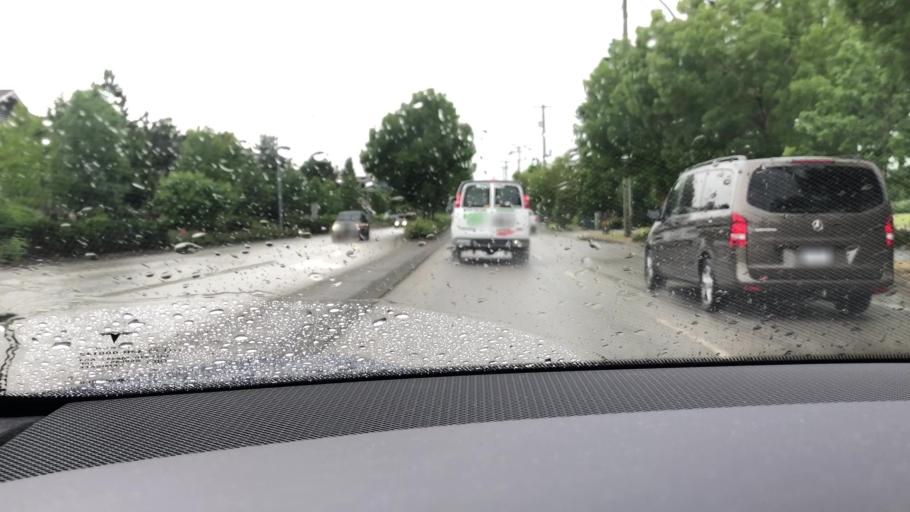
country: CA
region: British Columbia
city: Langley
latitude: 49.1335
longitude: -122.6650
